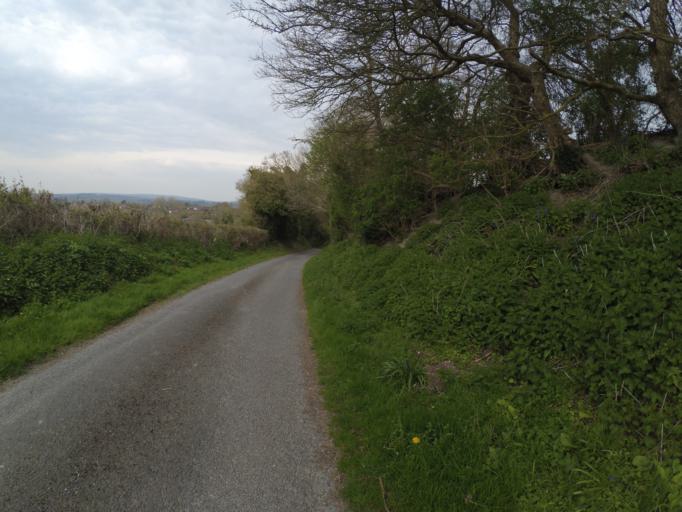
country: GB
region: England
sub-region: West Sussex
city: Arundel
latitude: 50.9045
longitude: -0.5334
